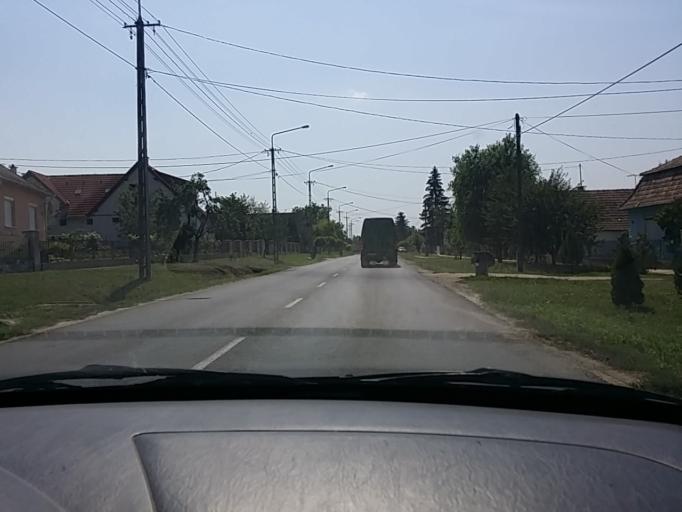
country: HU
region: Tolna
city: Iregszemcse
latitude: 46.7035
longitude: 18.1783
